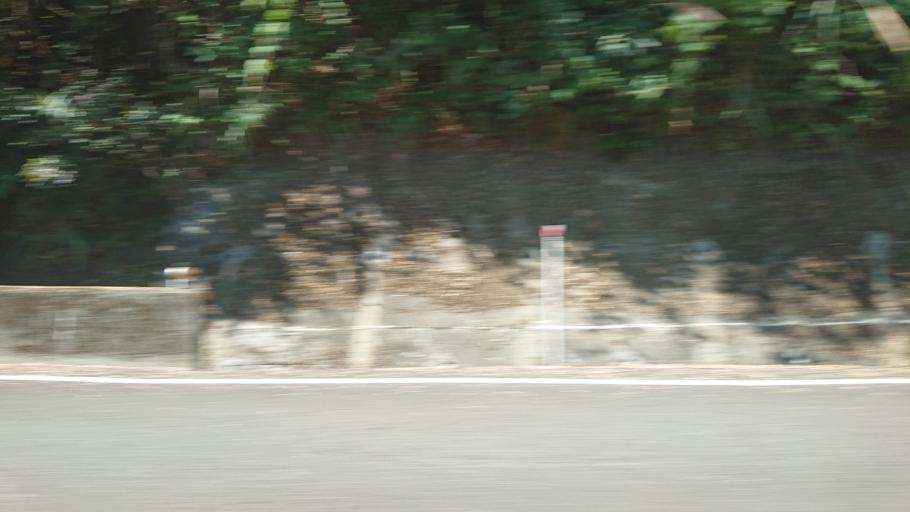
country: TW
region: Taiwan
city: Lugu
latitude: 23.4794
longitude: 120.7364
